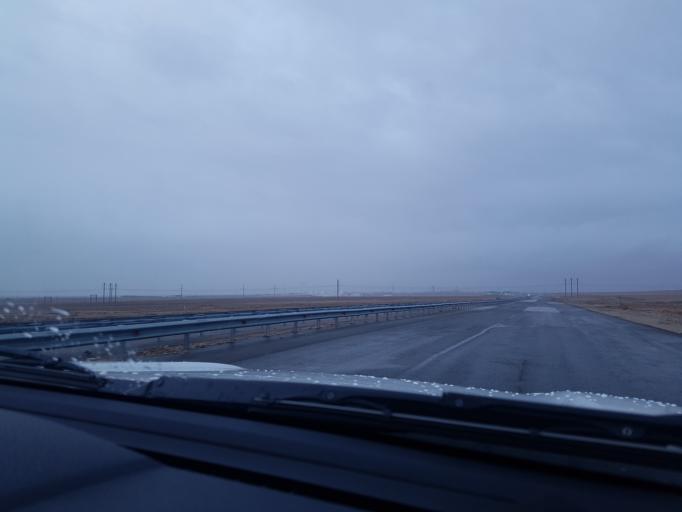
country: TM
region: Balkan
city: Balkanabat
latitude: 39.9238
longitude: 53.8723
